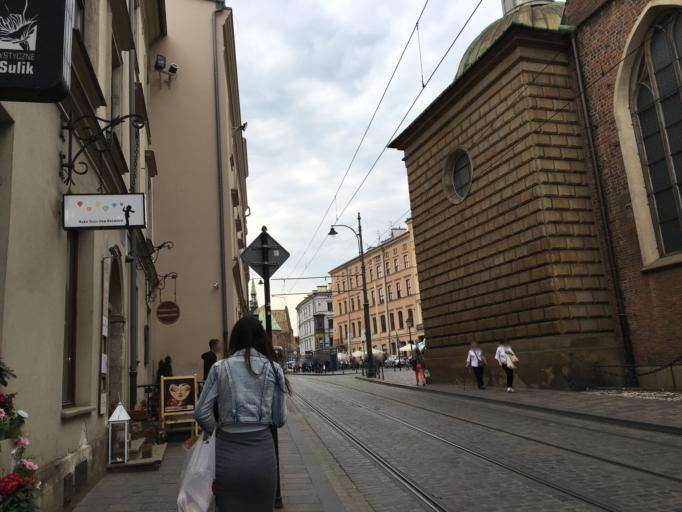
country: PL
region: Lesser Poland Voivodeship
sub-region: Krakow
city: Krakow
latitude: 50.0590
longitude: 19.9394
